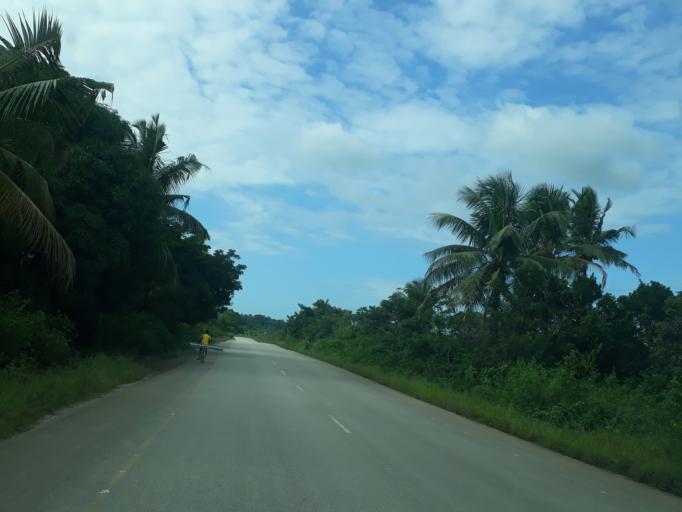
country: TZ
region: Zanzibar North
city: Kijini
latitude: -5.8386
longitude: 39.2863
